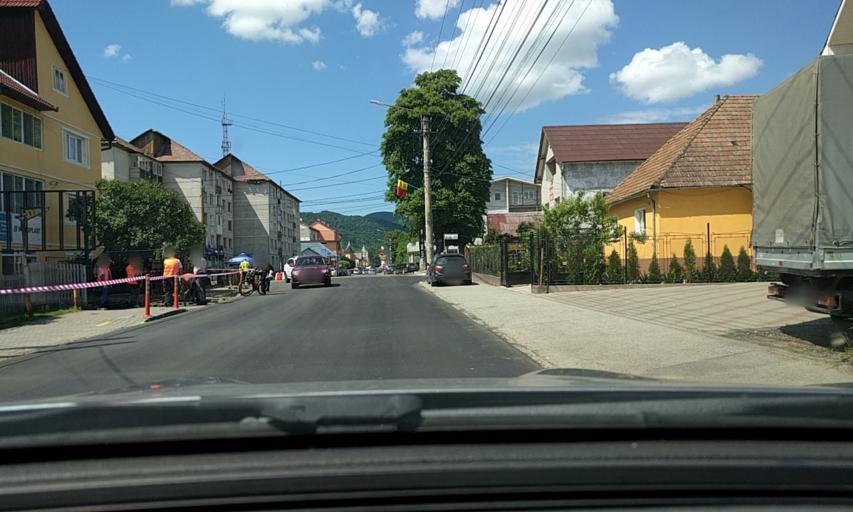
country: RO
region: Bistrita-Nasaud
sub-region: Oras Nasaud
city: Nasaud
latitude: 47.2842
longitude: 24.4200
